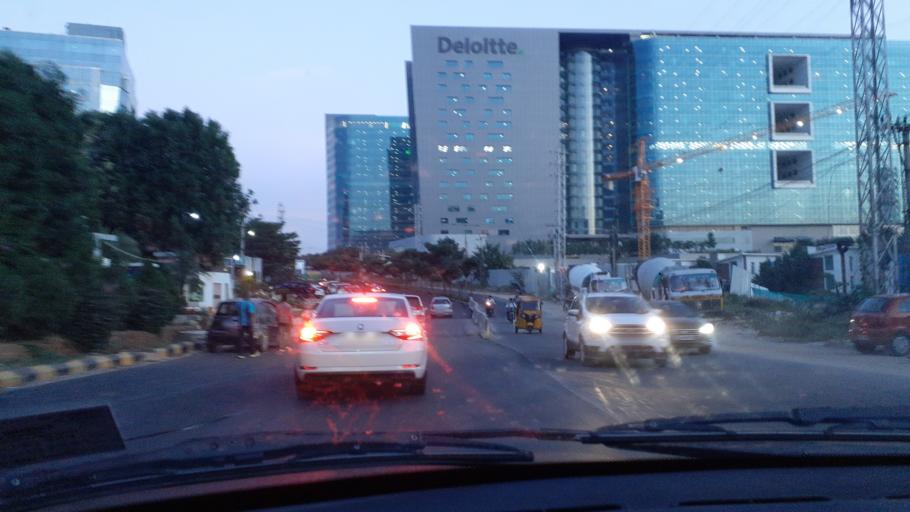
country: IN
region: Telangana
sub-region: Rangareddi
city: Kukatpalli
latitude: 17.4438
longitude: 78.3676
